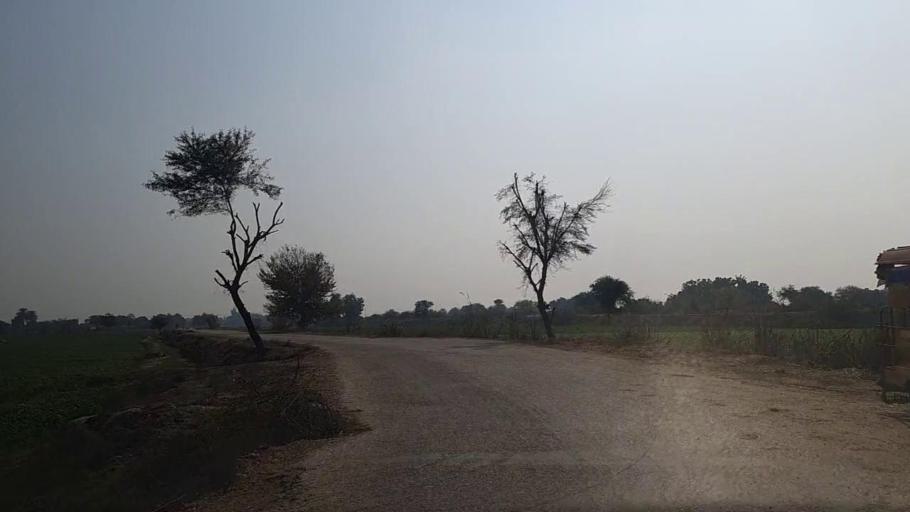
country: PK
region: Sindh
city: Jam Sahib
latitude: 26.3400
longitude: 68.5341
